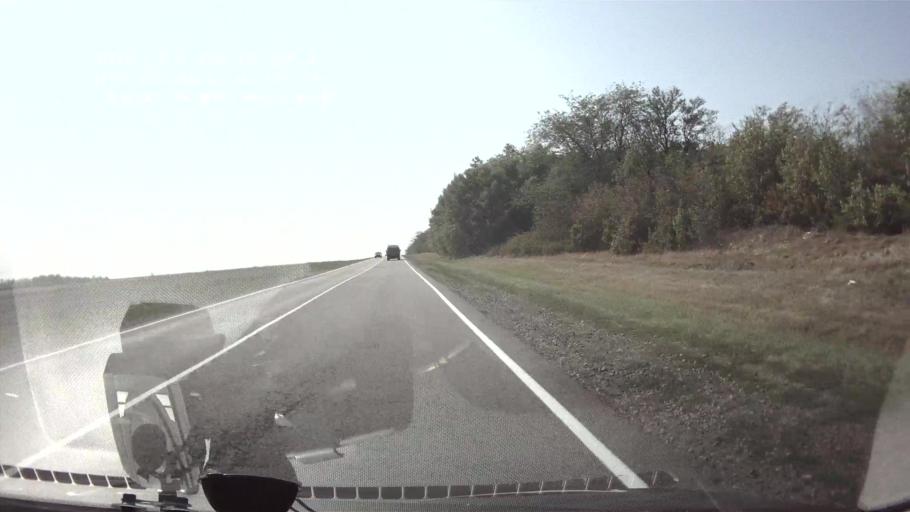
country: RU
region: Krasnodarskiy
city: Novopokrovskaya
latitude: 45.8332
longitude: 40.7202
